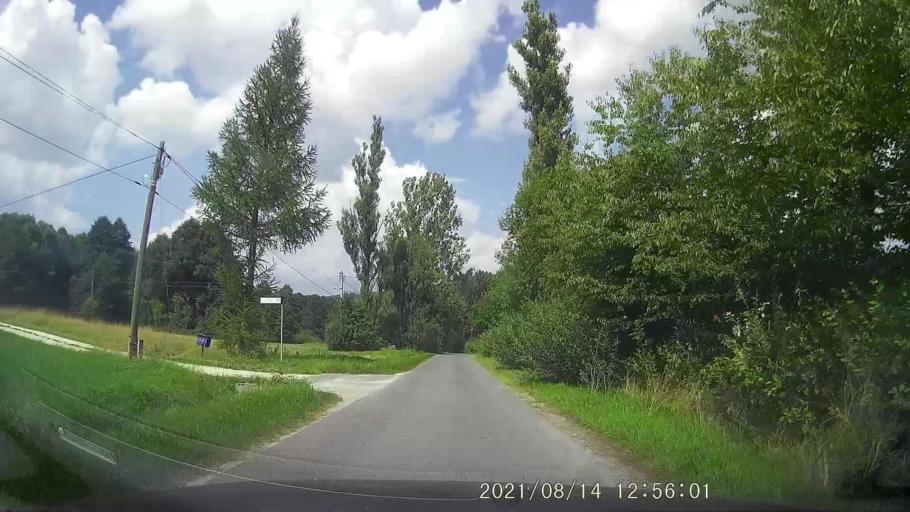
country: PL
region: Lower Silesian Voivodeship
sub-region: Powiat klodzki
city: Ladek-Zdroj
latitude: 50.3336
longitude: 16.8340
